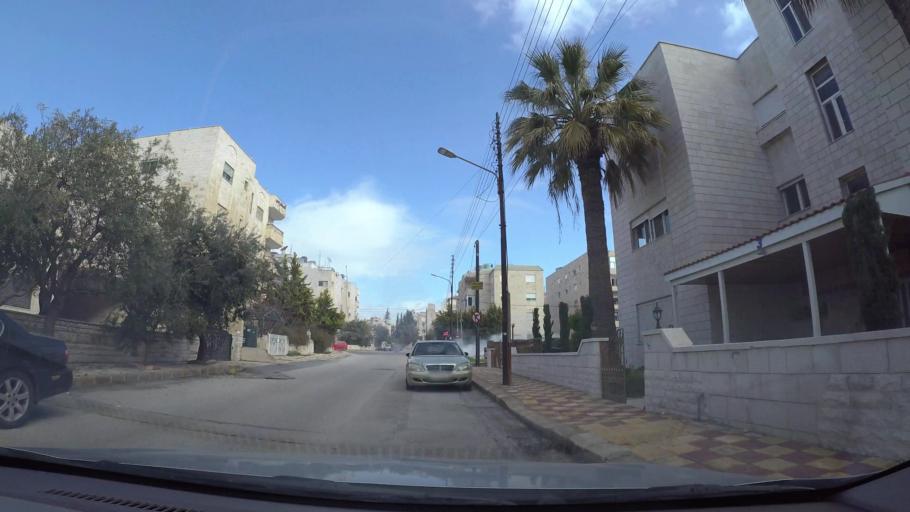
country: JO
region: Amman
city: Al Jubayhah
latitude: 31.9979
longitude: 35.8460
